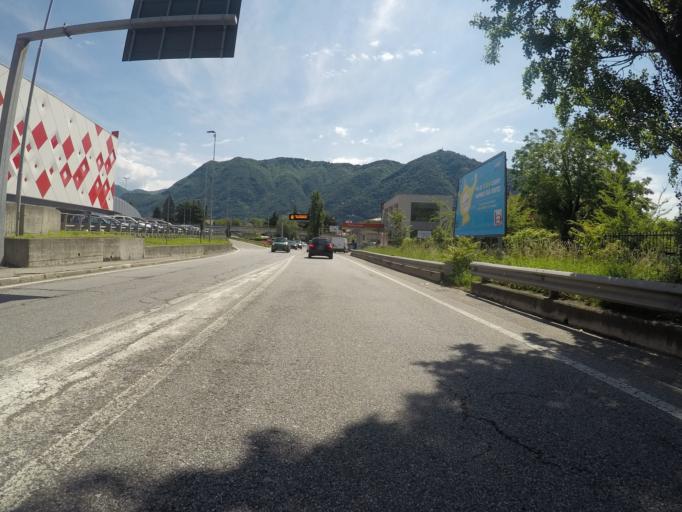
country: IT
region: Lombardy
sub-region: Provincia di Como
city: Cernobbio
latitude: 45.8366
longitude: 9.0648
